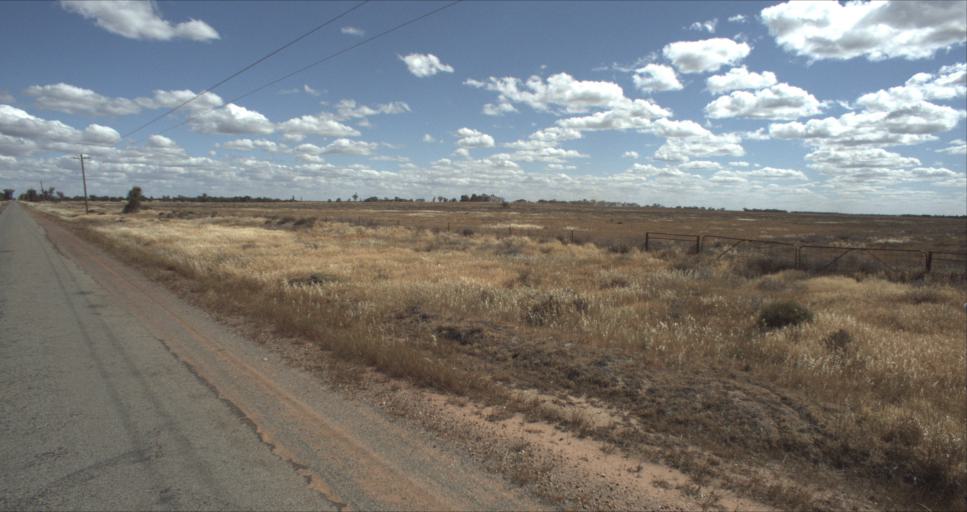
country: AU
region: New South Wales
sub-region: Leeton
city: Leeton
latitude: -34.4754
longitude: 146.2501
